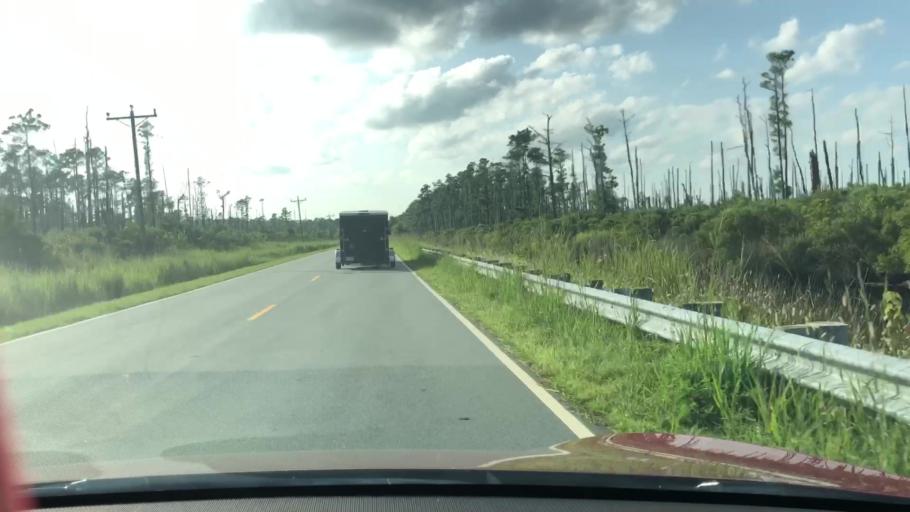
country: US
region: North Carolina
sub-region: Dare County
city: Wanchese
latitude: 35.6097
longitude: -75.8216
